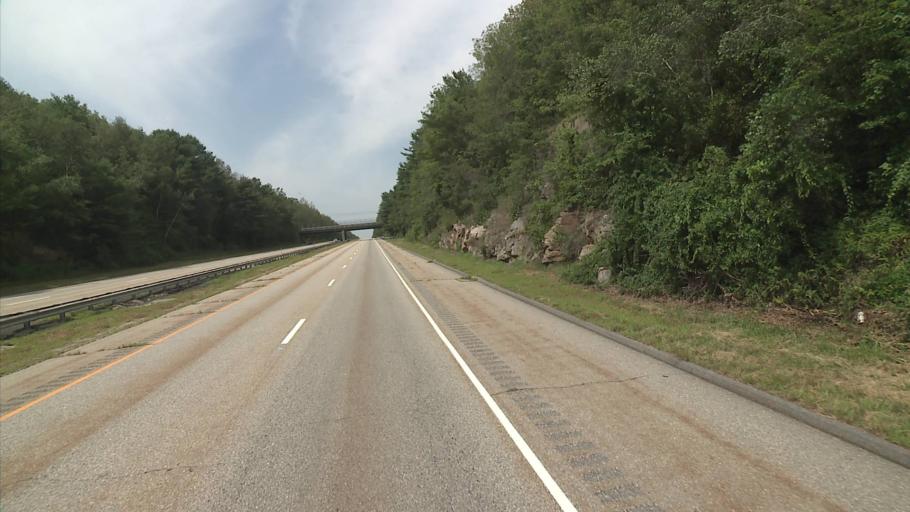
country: US
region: Connecticut
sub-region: Windham County
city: Danielson
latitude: 41.7871
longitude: -71.8096
